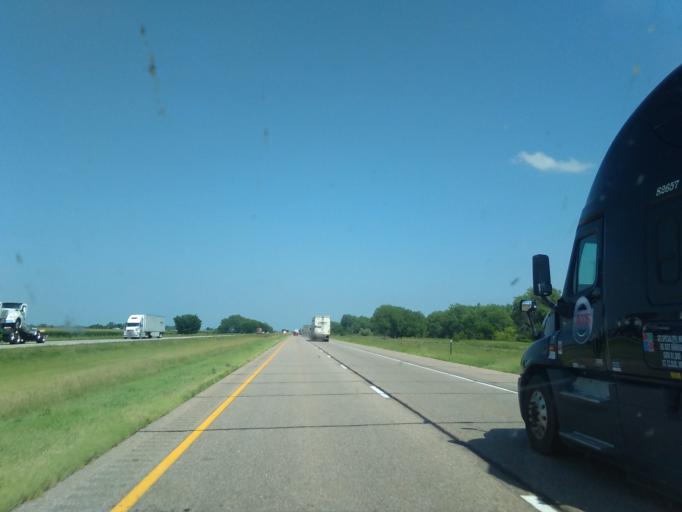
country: US
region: Nebraska
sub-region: Buffalo County
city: Kearney
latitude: 40.6722
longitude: -99.2077
